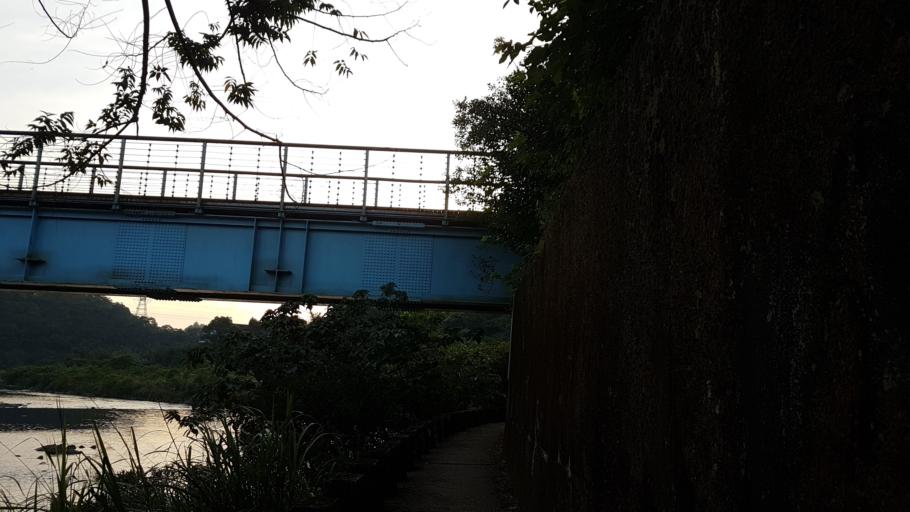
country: TW
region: Taiwan
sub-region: Yilan
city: Yilan
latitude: 24.9348
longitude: 121.7000
